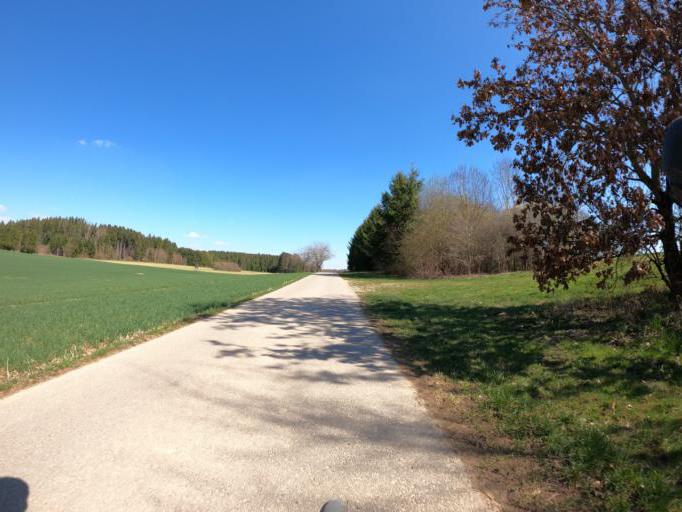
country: DE
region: Baden-Wuerttemberg
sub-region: Karlsruhe Region
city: Empfingen
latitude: 48.4047
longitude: 8.7075
